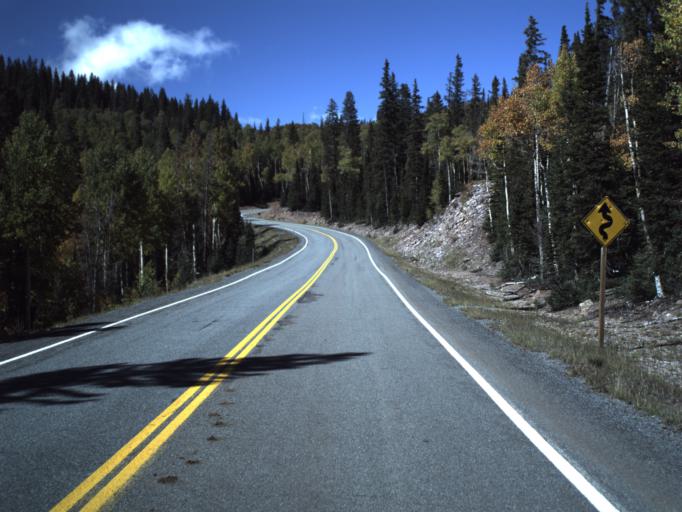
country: US
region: Utah
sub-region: Piute County
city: Junction
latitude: 38.3148
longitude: -112.3676
